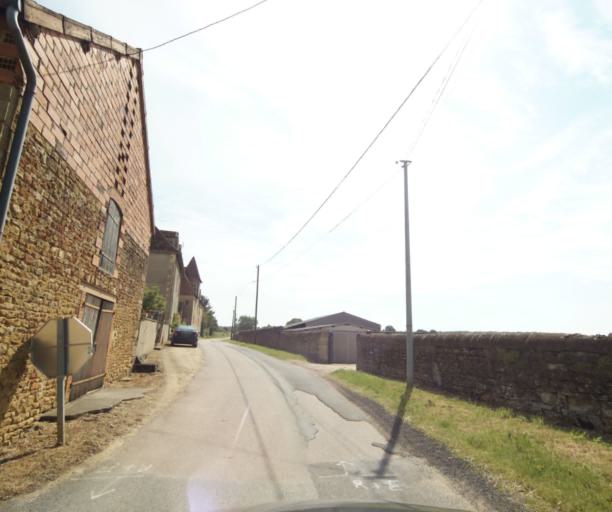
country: FR
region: Bourgogne
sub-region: Departement de Saone-et-Loire
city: Palinges
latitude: 46.5423
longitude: 4.1456
